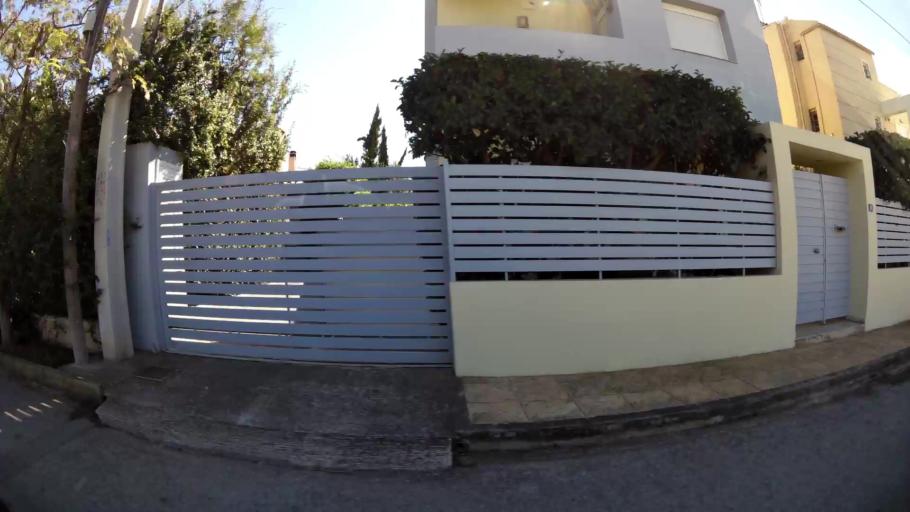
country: GR
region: Attica
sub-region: Nomarchia Anatolikis Attikis
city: Vari
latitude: 37.8354
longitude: 23.8195
